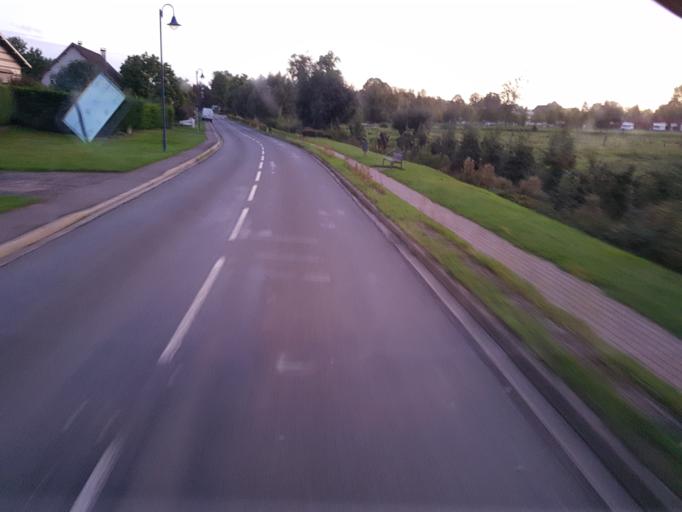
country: FR
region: Picardie
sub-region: Departement de la Somme
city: Ailly-sur-Noye
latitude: 49.7496
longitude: 2.3575
